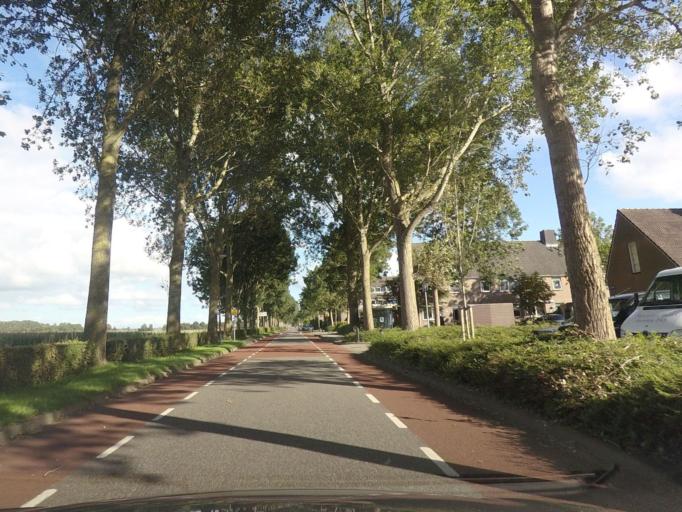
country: NL
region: North Holland
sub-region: Gemeente Alkmaar
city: Alkmaar
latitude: 52.6758
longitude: 4.7574
